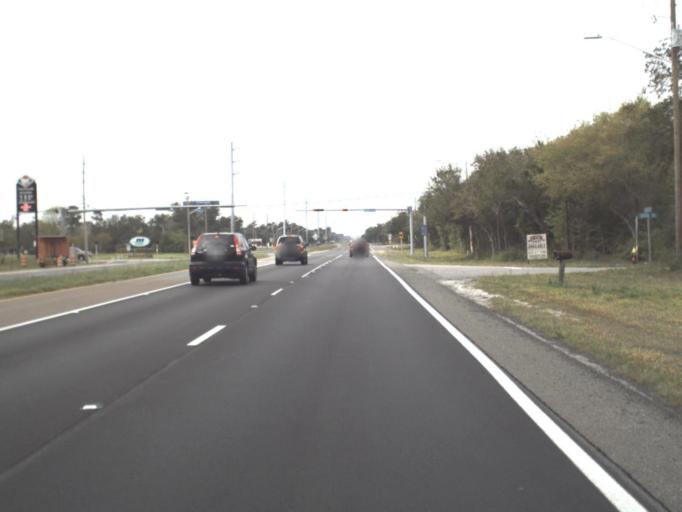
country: US
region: Florida
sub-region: Santa Rosa County
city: Woodlawn Beach
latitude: 30.3978
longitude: -87.0141
